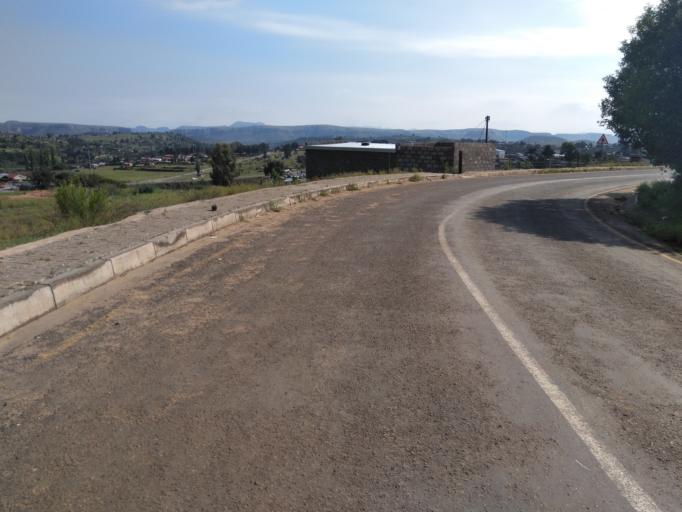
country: LS
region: Butha-Buthe
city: Butha-Buthe
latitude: -28.7750
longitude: 28.2462
